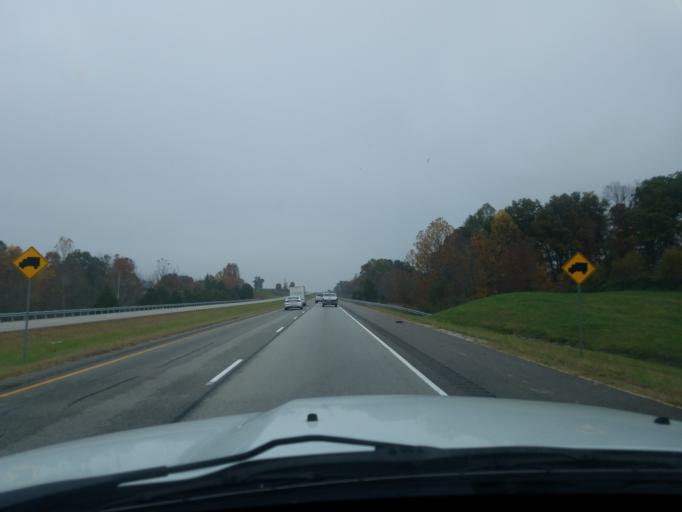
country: US
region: Kentucky
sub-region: Hardin County
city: Elizabethtown
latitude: 37.6451
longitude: -85.8379
